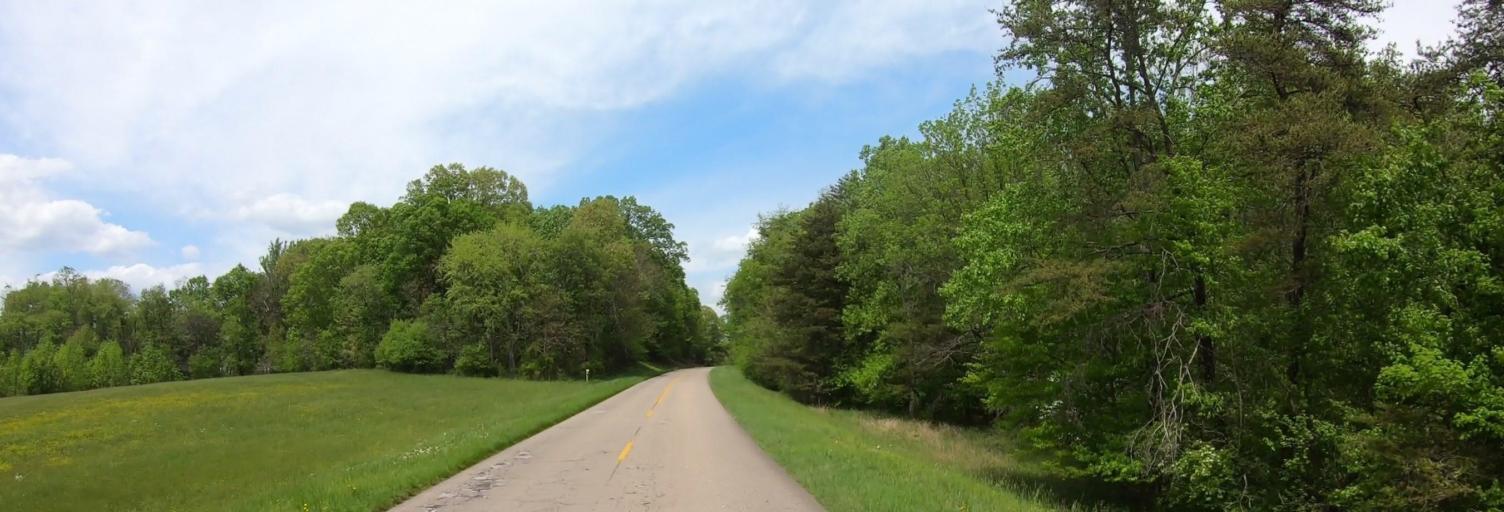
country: US
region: Virginia
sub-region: Roanoke County
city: Vinton
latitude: 37.2682
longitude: -79.8567
